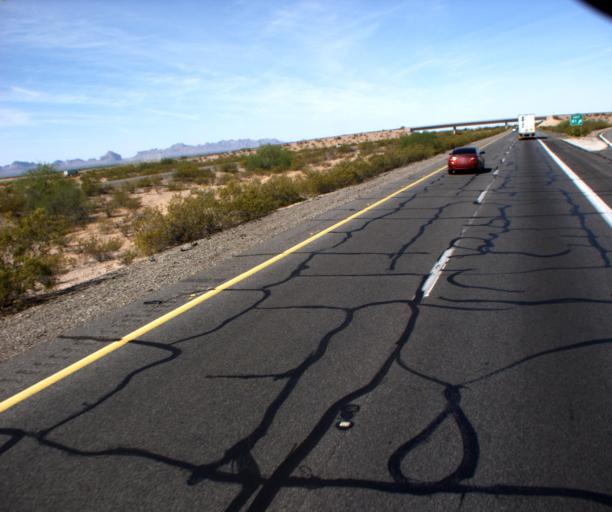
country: US
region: Arizona
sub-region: La Paz County
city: Salome
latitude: 33.5369
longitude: -113.1506
